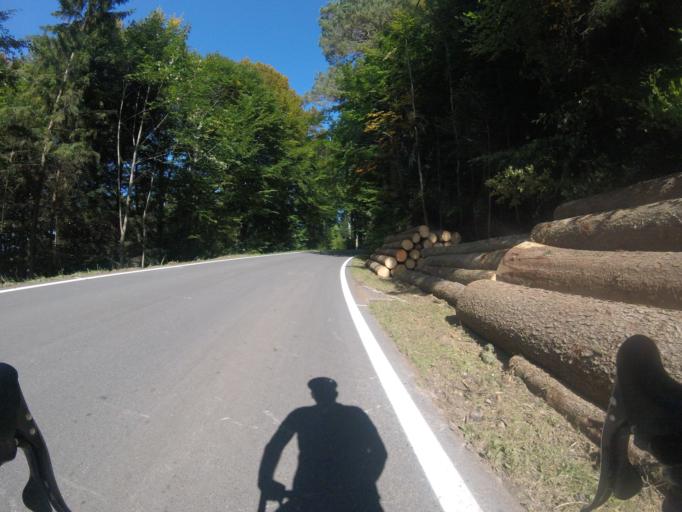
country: CH
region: Bern
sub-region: Bern-Mittelland District
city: Toffen
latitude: 46.8691
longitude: 7.5132
